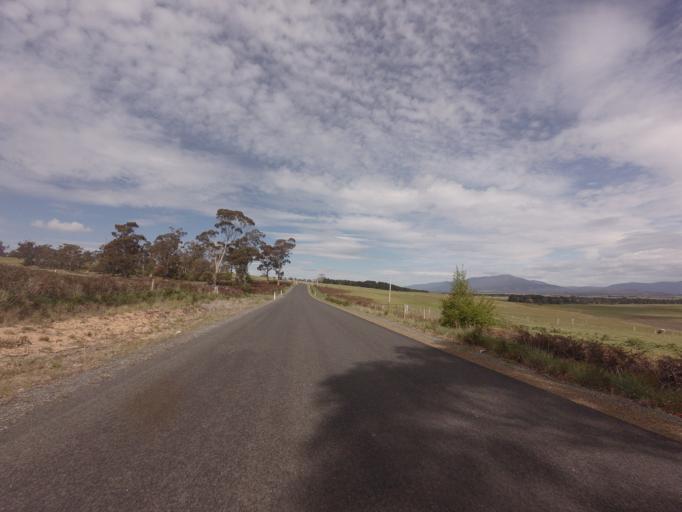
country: AU
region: Tasmania
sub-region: Northern Midlands
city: Longford
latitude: -41.7639
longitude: 147.2107
